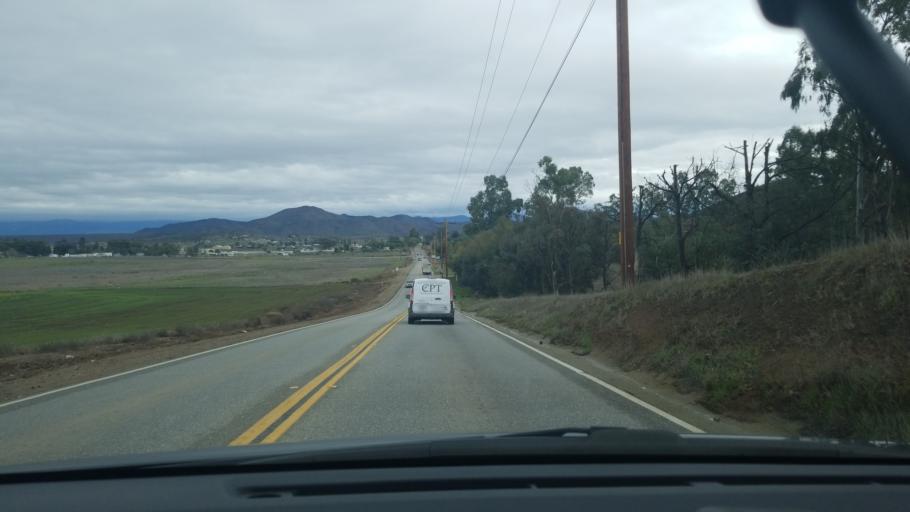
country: US
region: California
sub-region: Riverside County
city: Winchester
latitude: 33.6416
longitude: -117.1255
